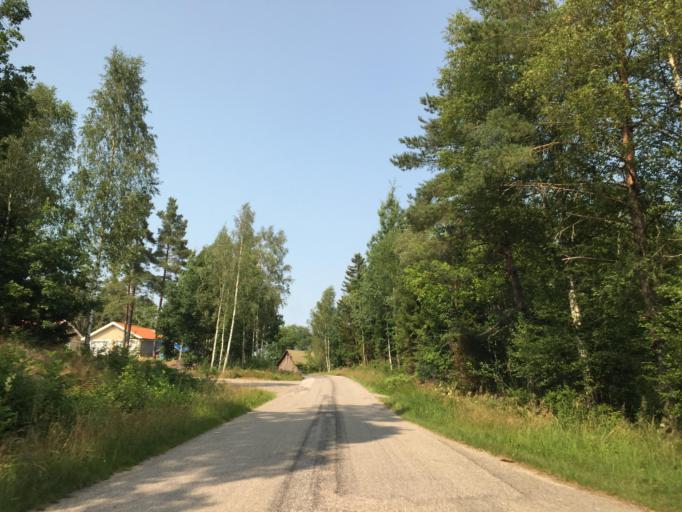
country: SE
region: Vaestra Goetaland
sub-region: Trollhattan
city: Sjuntorp
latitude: 58.2970
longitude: 12.1445
